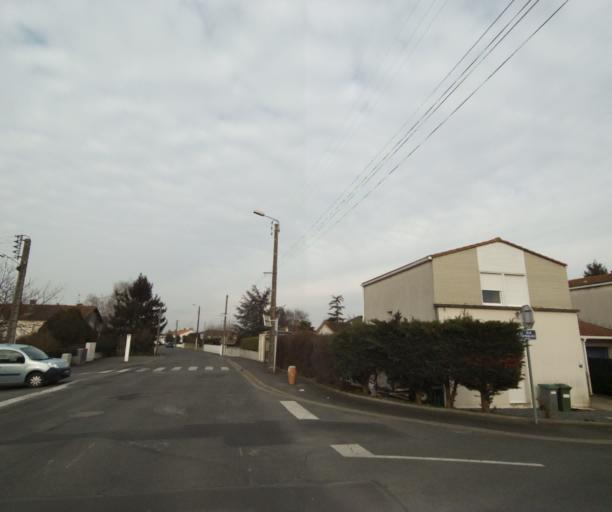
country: FR
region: Poitou-Charentes
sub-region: Departement des Deux-Sevres
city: Niort
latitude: 46.3107
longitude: -0.4544
